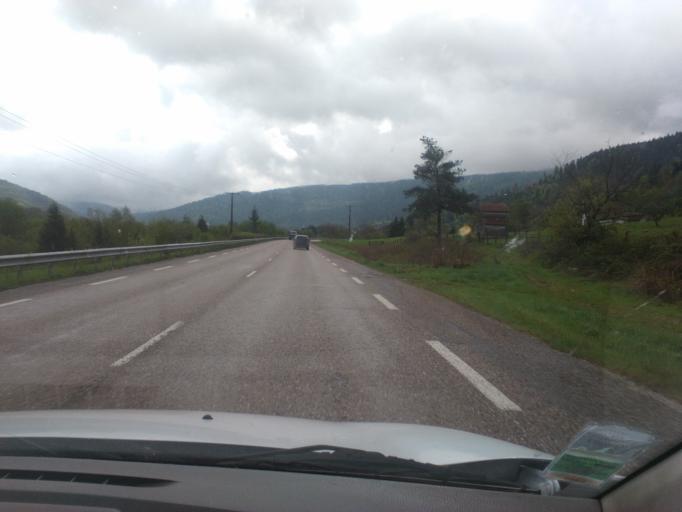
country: FR
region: Lorraine
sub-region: Departement des Vosges
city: Saulxures-sur-Moselotte
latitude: 47.9499
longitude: 6.7493
